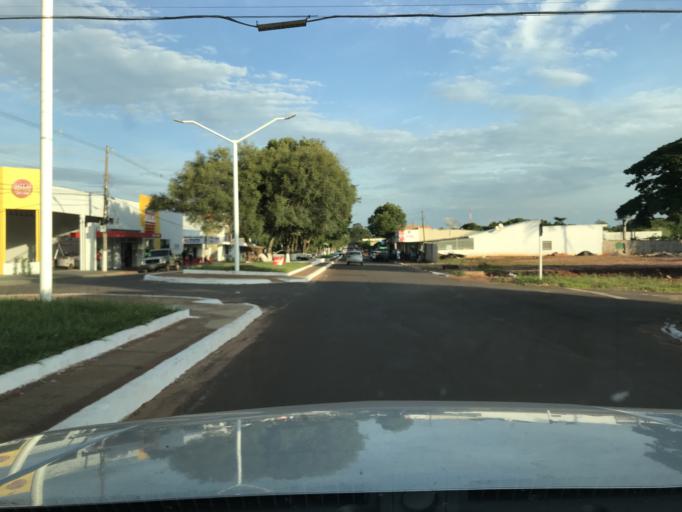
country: BR
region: Mato Grosso do Sul
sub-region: Iguatemi
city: Iguatemi
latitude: -23.6656
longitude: -54.5624
